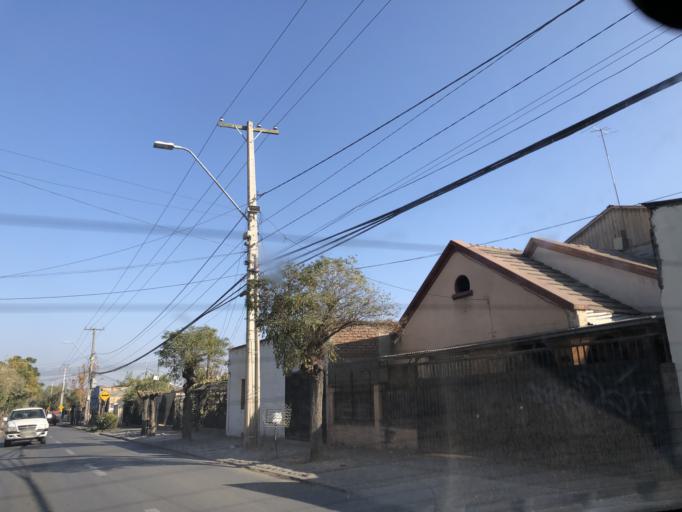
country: CL
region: Santiago Metropolitan
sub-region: Provincia de Cordillera
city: Puente Alto
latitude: -33.6218
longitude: -70.5750
